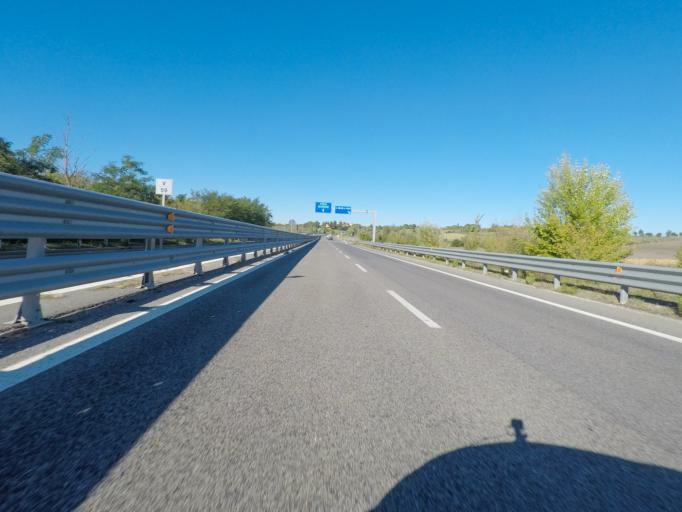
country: IT
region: Tuscany
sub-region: Provincia di Siena
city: Rosia
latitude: 43.2370
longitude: 11.2790
